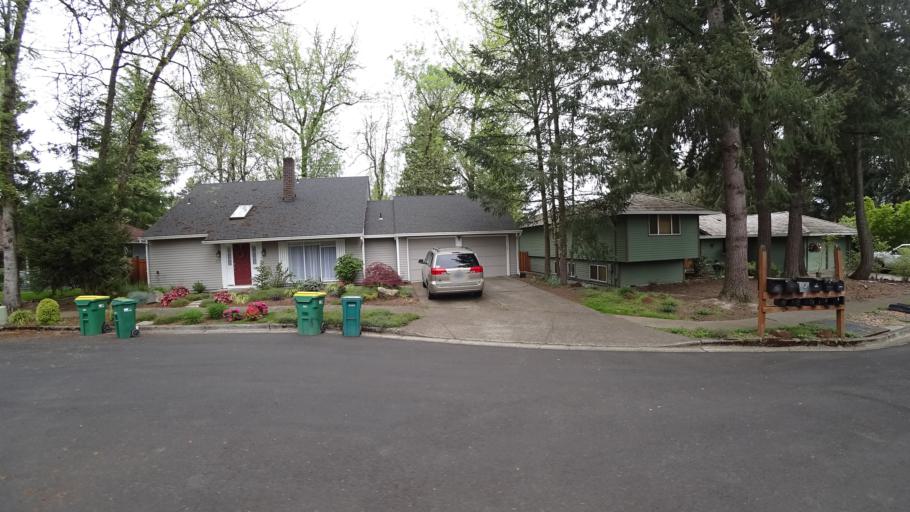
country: US
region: Oregon
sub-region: Washington County
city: Beaverton
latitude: 45.4564
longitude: -122.8188
